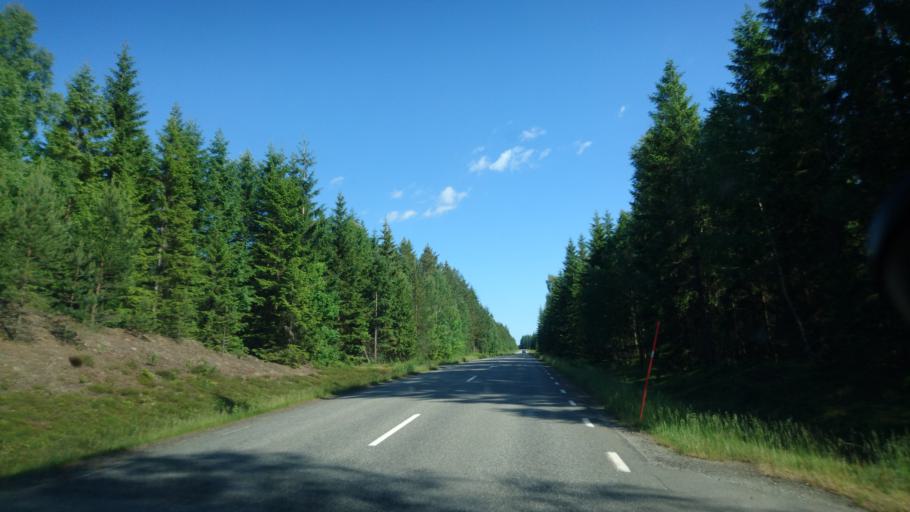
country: SE
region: Skane
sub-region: Osby Kommun
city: Lonsboda
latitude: 56.4381
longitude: 14.2503
